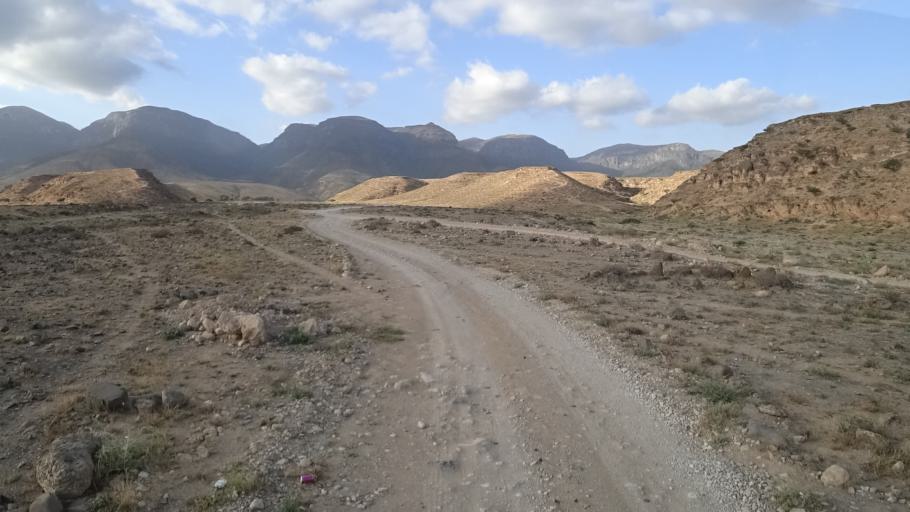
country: OM
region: Zufar
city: Salalah
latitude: 16.9783
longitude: 53.8532
